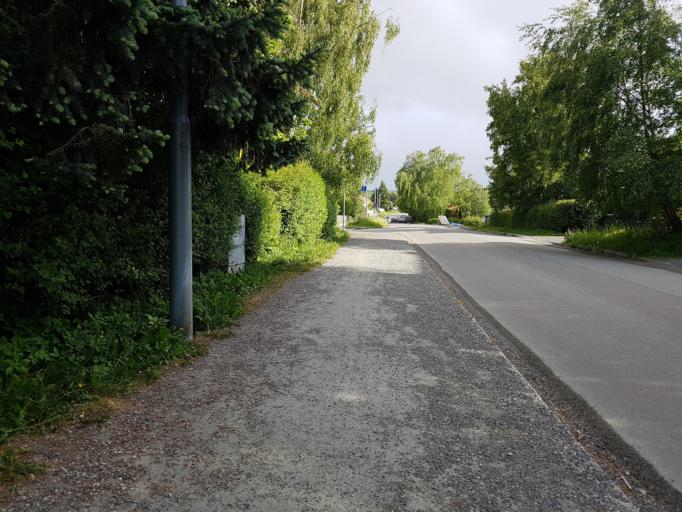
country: NO
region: Sor-Trondelag
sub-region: Trondheim
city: Trondheim
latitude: 63.4296
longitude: 10.4605
